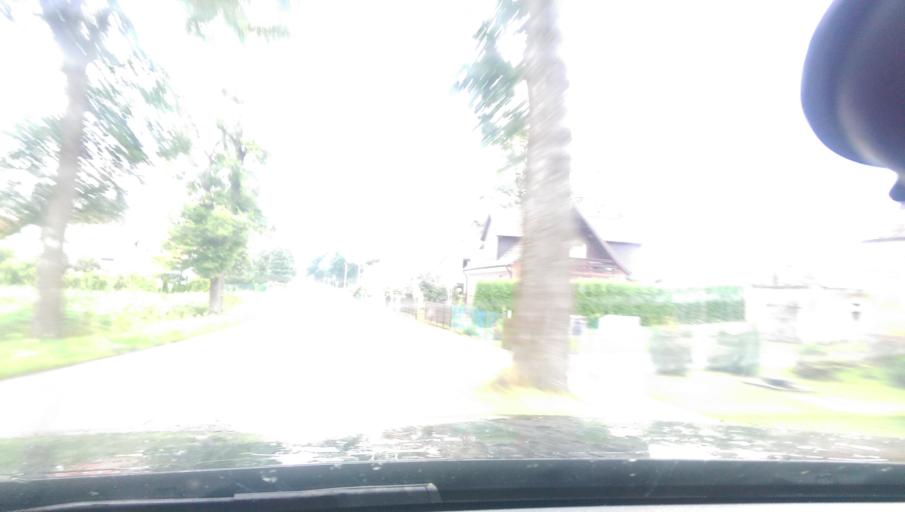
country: PL
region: Warmian-Masurian Voivodeship
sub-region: Powiat piski
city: Ruciane-Nida
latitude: 53.6882
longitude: 21.4898
